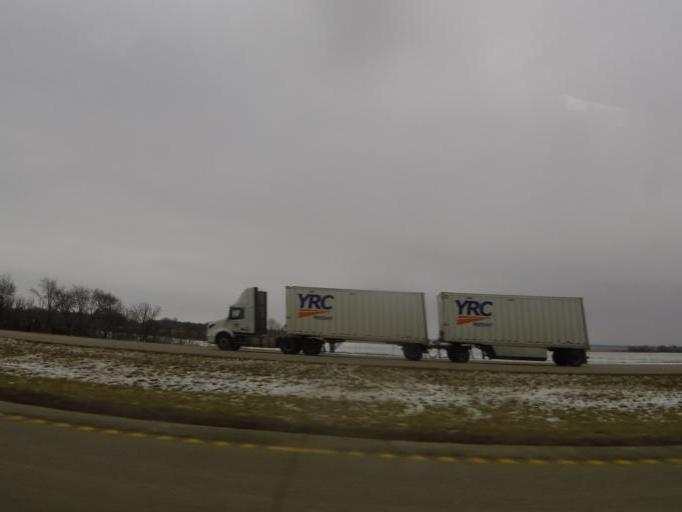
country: US
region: Missouri
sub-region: Clark County
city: Kahoka
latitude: 40.3578
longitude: -91.5870
